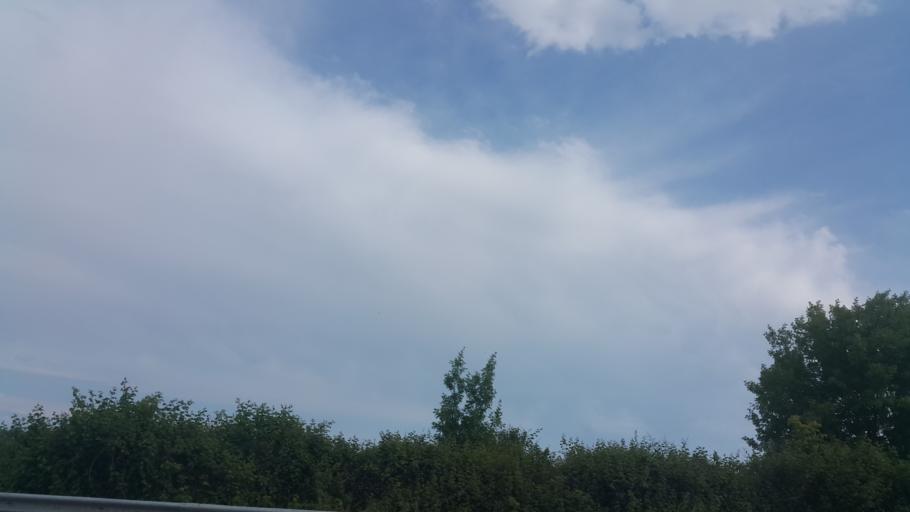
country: TR
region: Mersin
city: Kazanli
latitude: 36.9197
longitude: 34.6941
